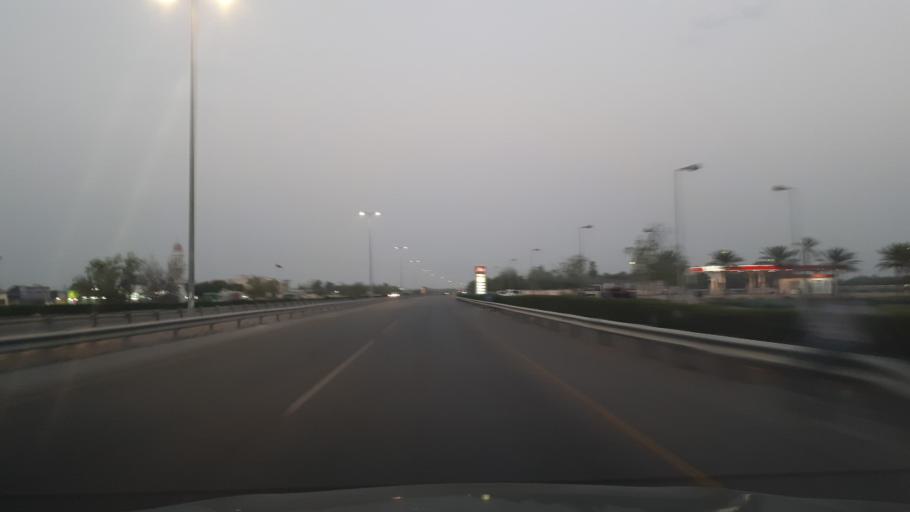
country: OM
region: Al Batinah
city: Barka'
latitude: 23.7351
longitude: 57.6762
